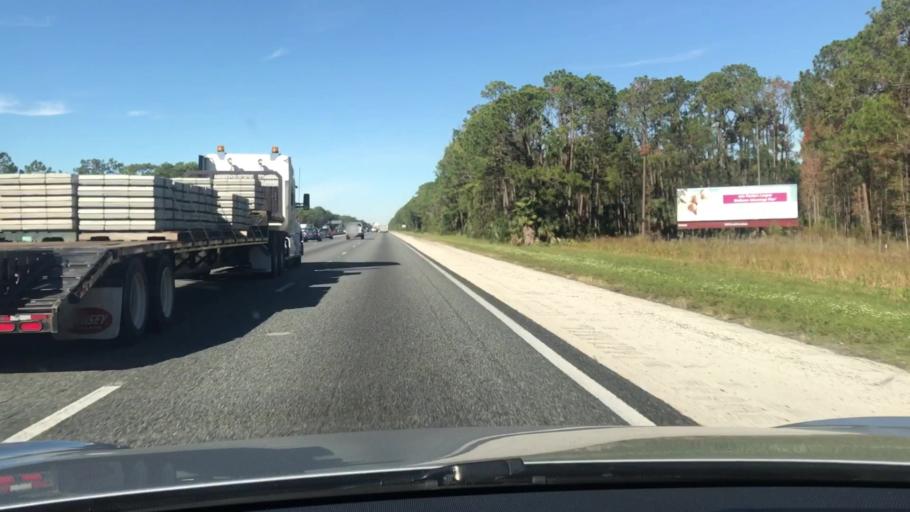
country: US
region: Florida
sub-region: Volusia County
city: Ormond-by-the-Sea
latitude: 29.3551
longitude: -81.1339
